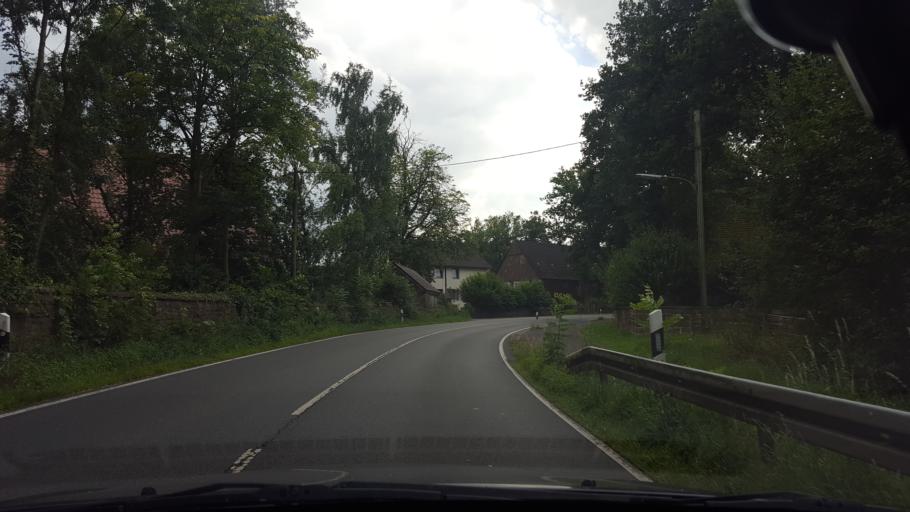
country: DE
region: North Rhine-Westphalia
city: Oer-Erkenschwick
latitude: 51.6432
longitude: 7.2331
